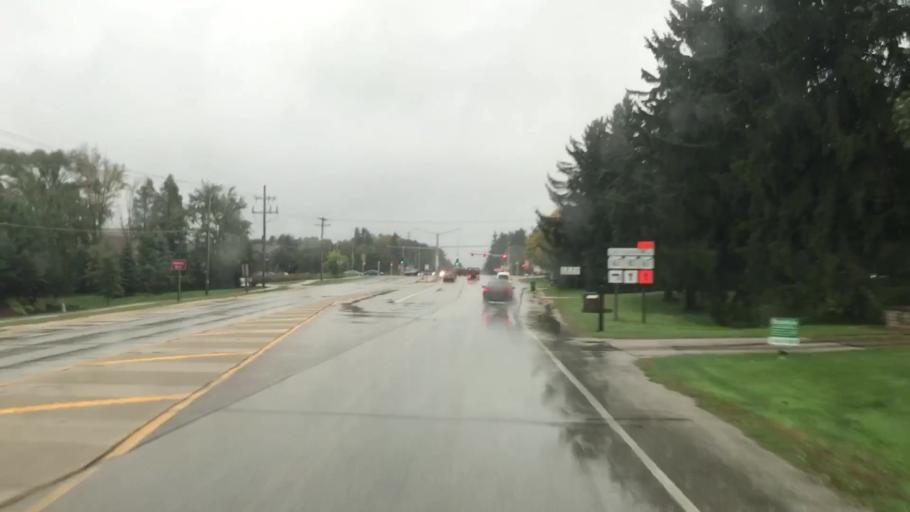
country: US
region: Wisconsin
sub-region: Ozaukee County
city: Mequon
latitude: 43.2236
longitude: -88.0036
